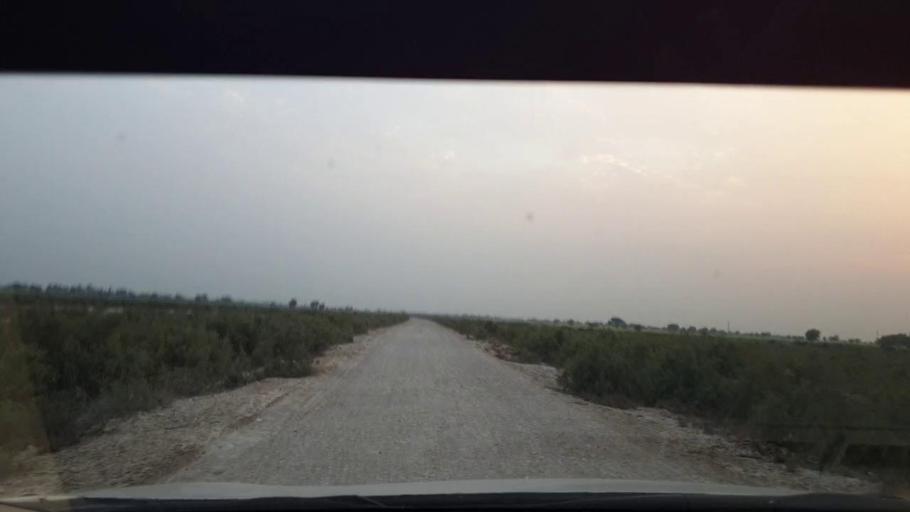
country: PK
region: Sindh
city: Berani
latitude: 25.8767
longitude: 68.7620
